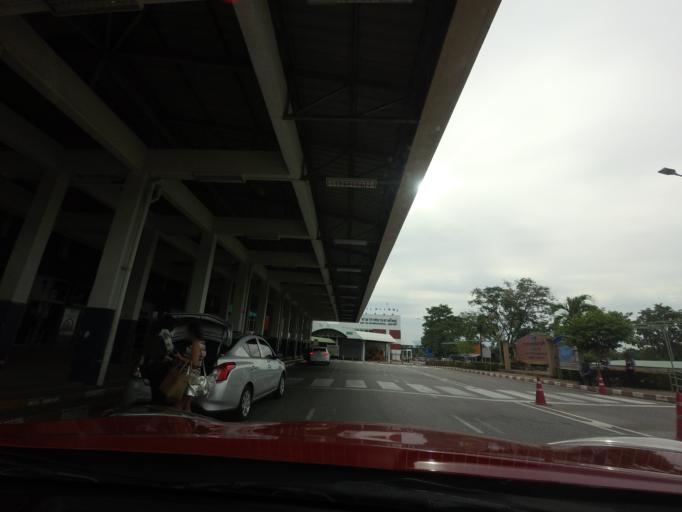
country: TH
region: Songkhla
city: Khlong Hoi Khong
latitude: 6.9368
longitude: 100.3947
